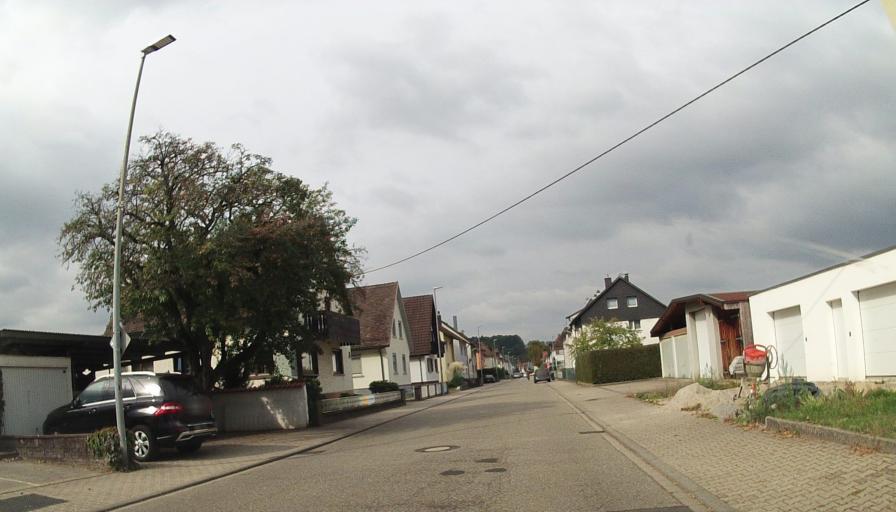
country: DE
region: Baden-Wuerttemberg
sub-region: Karlsruhe Region
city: Gaggenau
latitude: 48.7903
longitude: 8.3346
